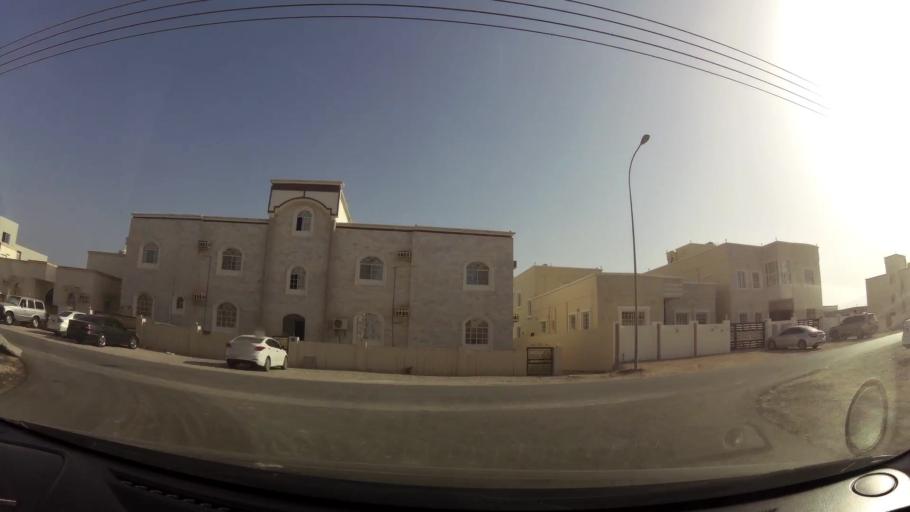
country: OM
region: Zufar
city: Salalah
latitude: 17.0152
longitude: 54.0146
